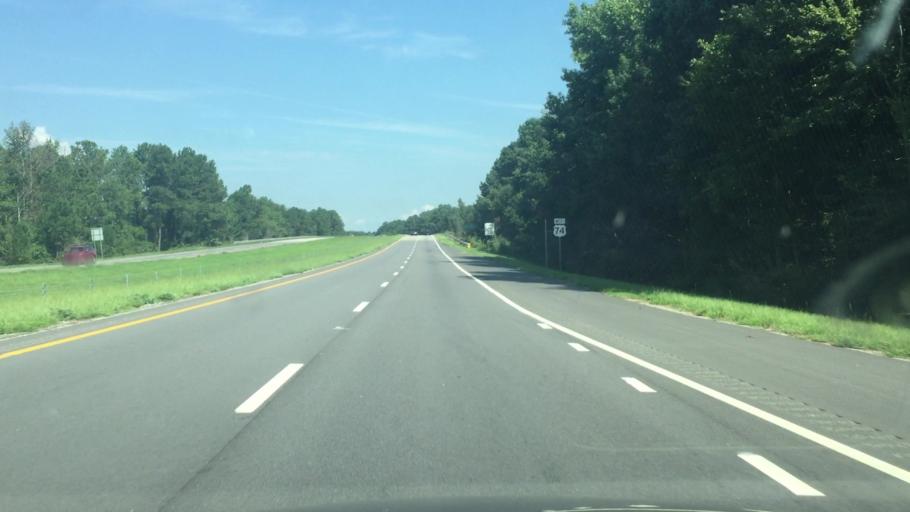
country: US
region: North Carolina
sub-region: Robeson County
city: Maxton
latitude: 34.7223
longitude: -79.3141
